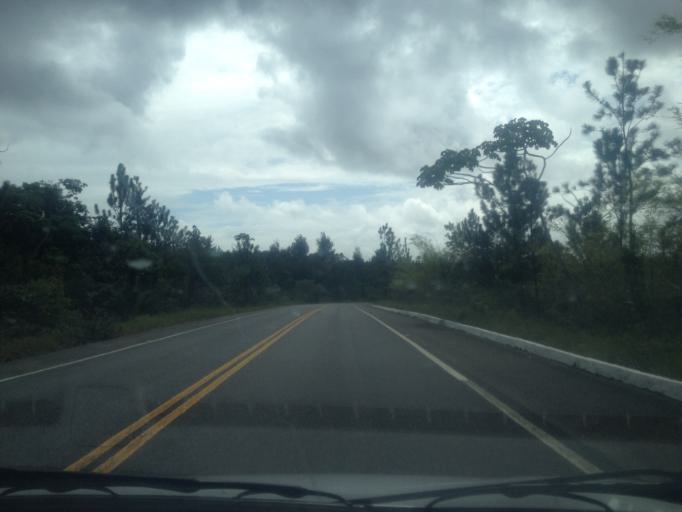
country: BR
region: Bahia
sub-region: Entre Rios
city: Entre Rios
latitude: -12.1322
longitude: -37.7918
